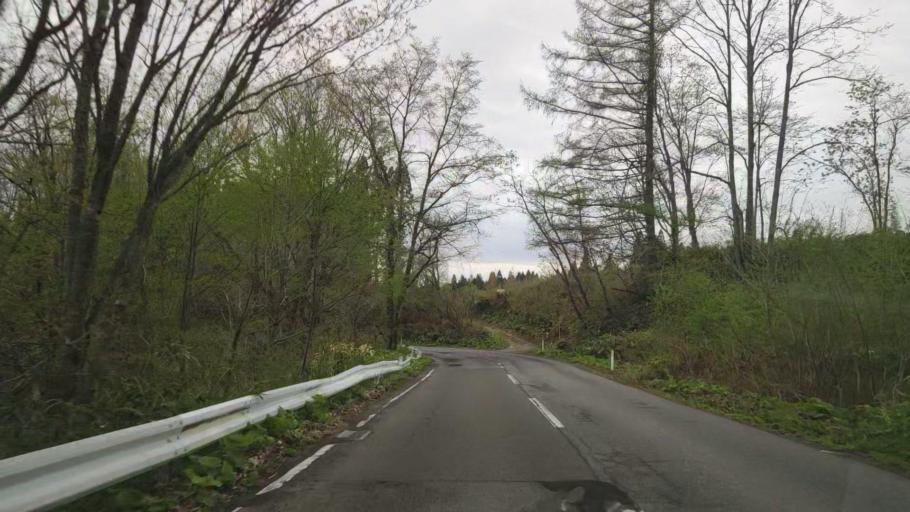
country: JP
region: Akita
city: Hanawa
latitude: 40.3766
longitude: 140.7898
